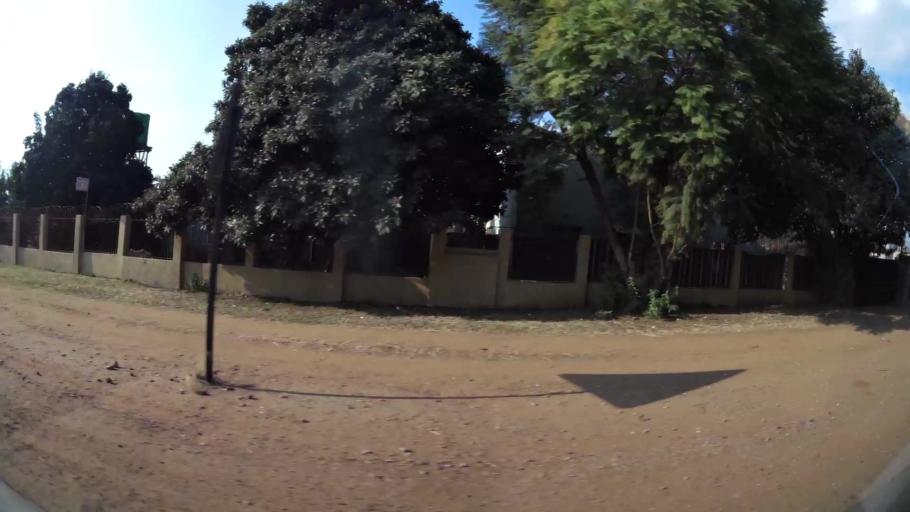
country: ZA
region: Gauteng
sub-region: Ekurhuleni Metropolitan Municipality
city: Benoni
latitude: -26.0925
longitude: 28.2952
